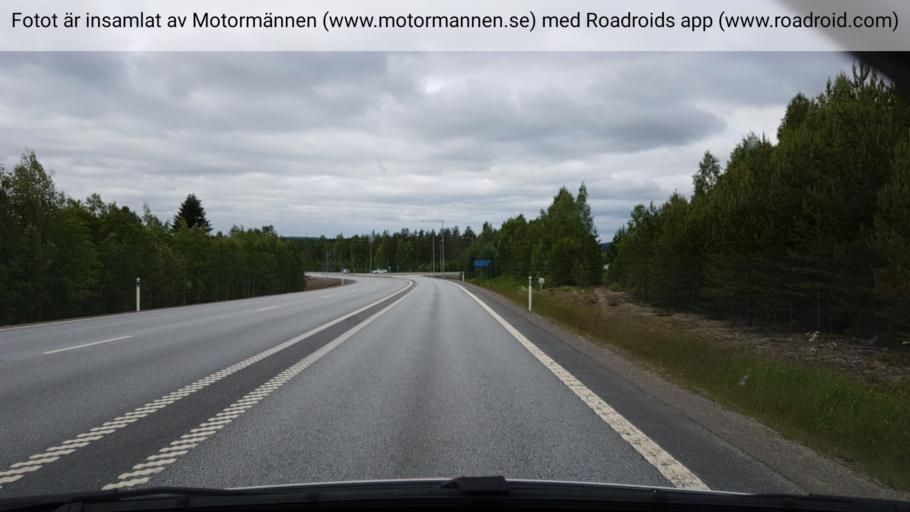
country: SE
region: Vaesterbotten
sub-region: Vannas Kommun
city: Vaennaes
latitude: 63.9215
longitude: 19.7865
